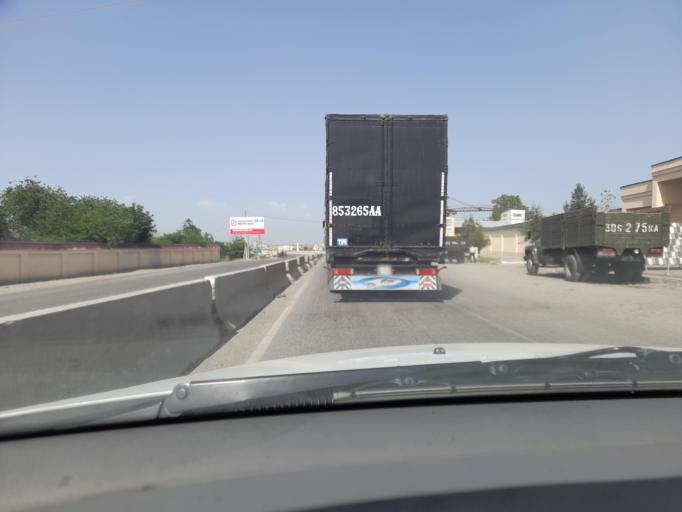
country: UZ
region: Samarqand
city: Samarqand
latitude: 39.6937
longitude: 67.0170
